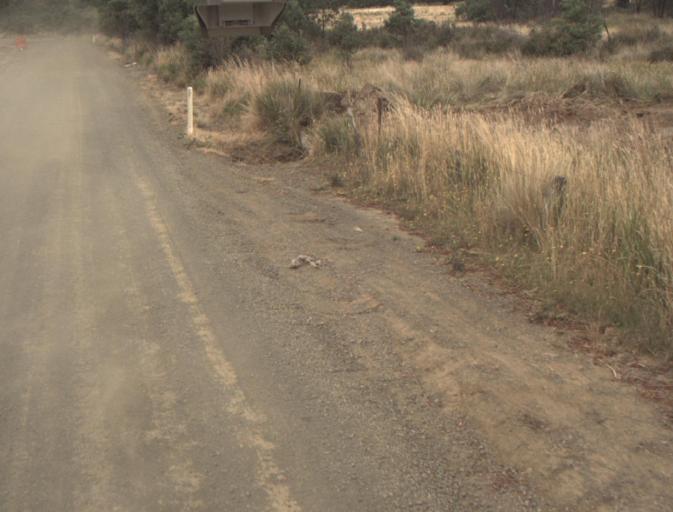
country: AU
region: Tasmania
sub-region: Northern Midlands
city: Evandale
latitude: -41.5155
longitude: 147.3508
